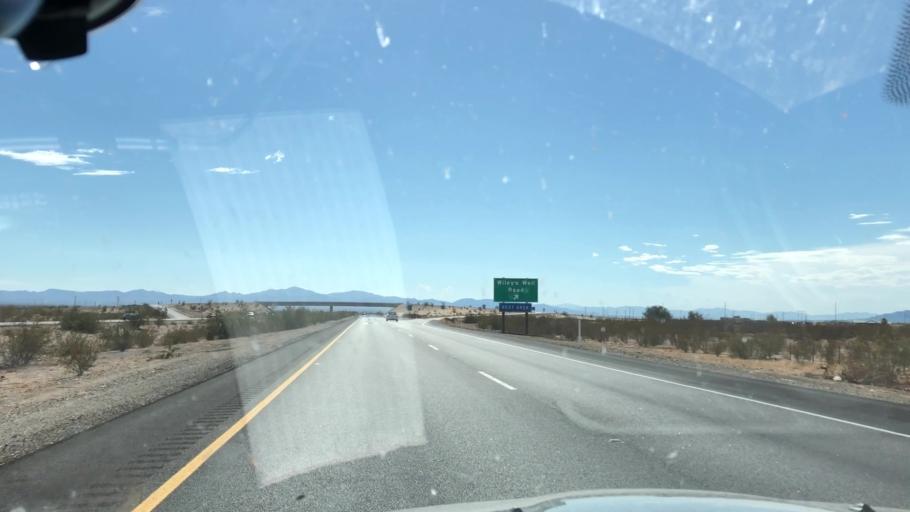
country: US
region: California
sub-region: Riverside County
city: Mesa Verde
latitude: 33.6082
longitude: -114.8961
